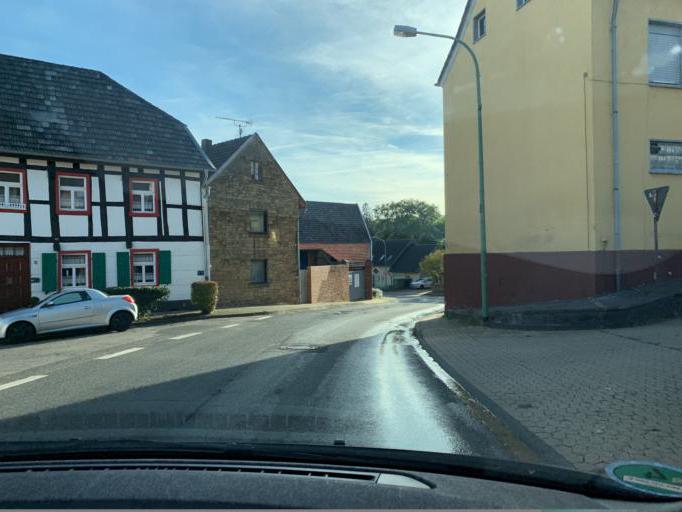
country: DE
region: North Rhine-Westphalia
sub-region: Regierungsbezirk Koln
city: Nideggen
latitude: 50.7056
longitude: 6.5201
